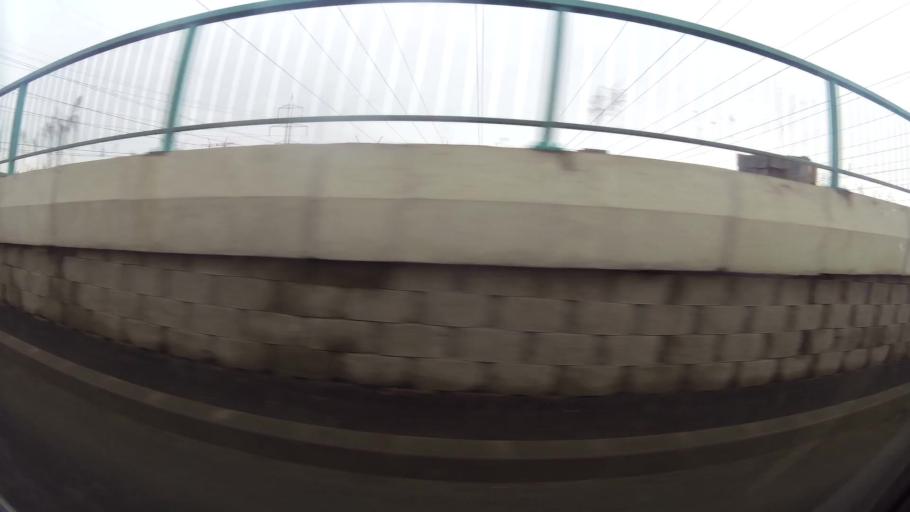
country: RO
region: Ilfov
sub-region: Comuna Popesti-Leordeni
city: Popesti-Leordeni
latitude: 44.4007
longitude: 26.1608
